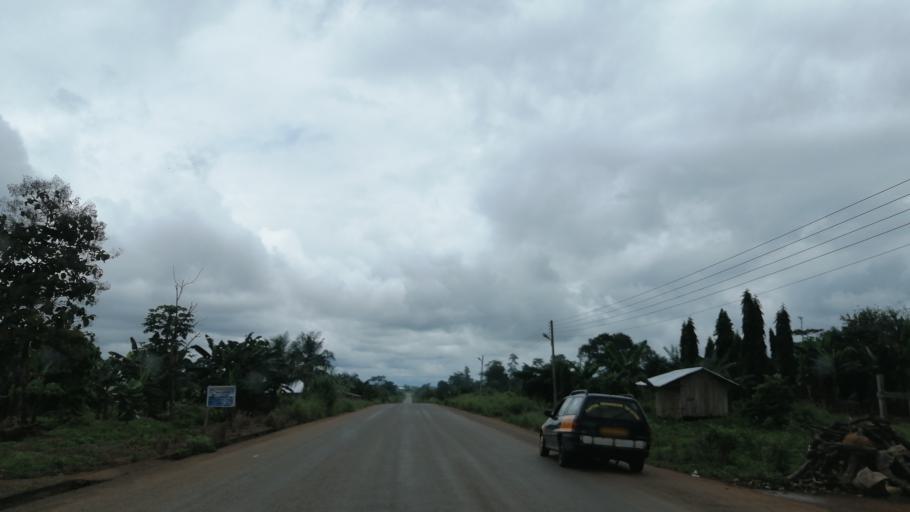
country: GH
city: Duayaw Nkwanta
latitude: 6.9131
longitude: -2.3879
